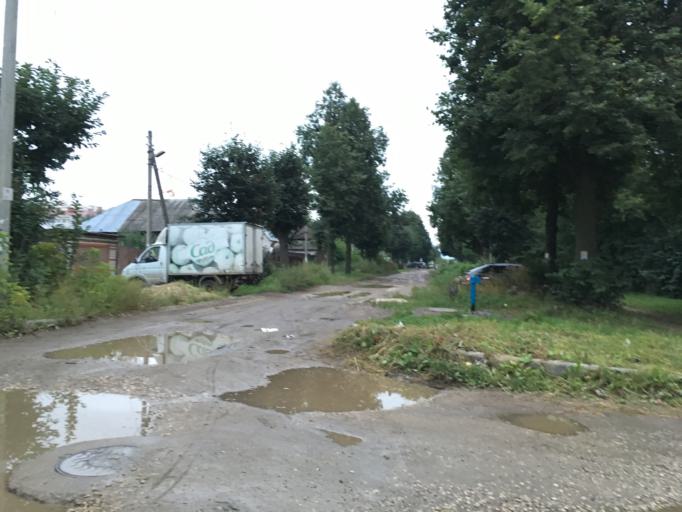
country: RU
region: Mariy-El
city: Yoshkar-Ola
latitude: 56.6489
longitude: 47.8891
